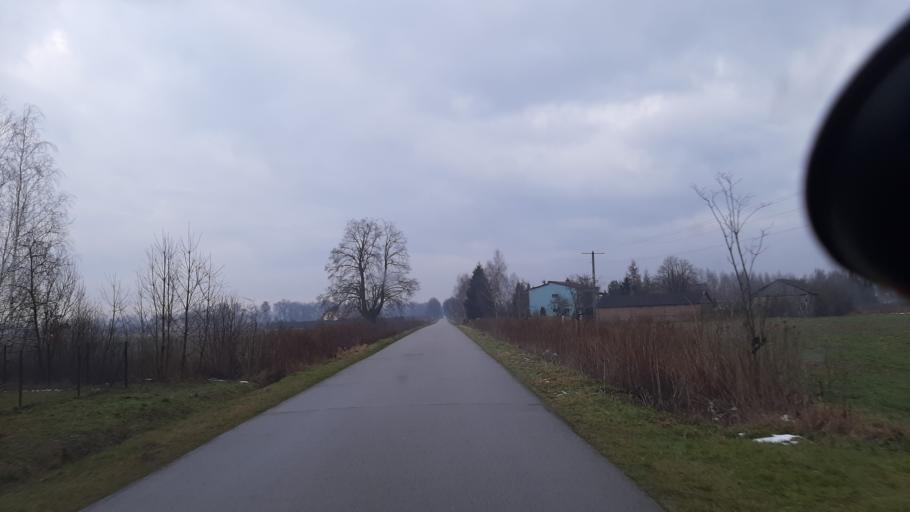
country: PL
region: Lublin Voivodeship
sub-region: Powiat lubelski
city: Lublin
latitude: 51.3376
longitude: 22.5431
